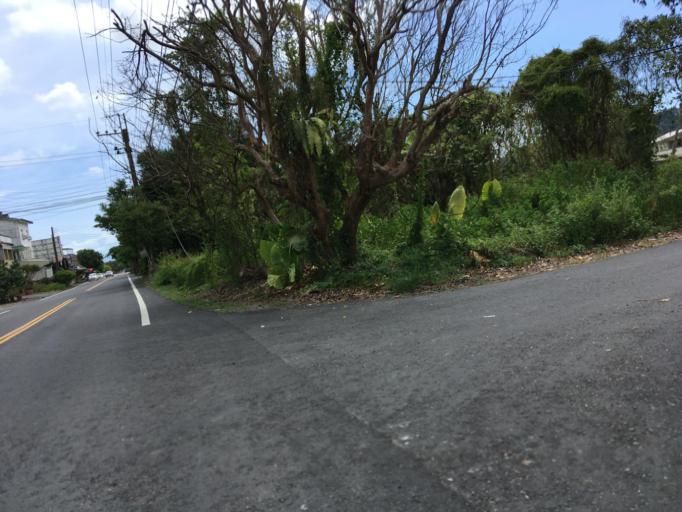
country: TW
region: Taiwan
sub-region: Yilan
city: Yilan
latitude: 24.6320
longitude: 121.7123
